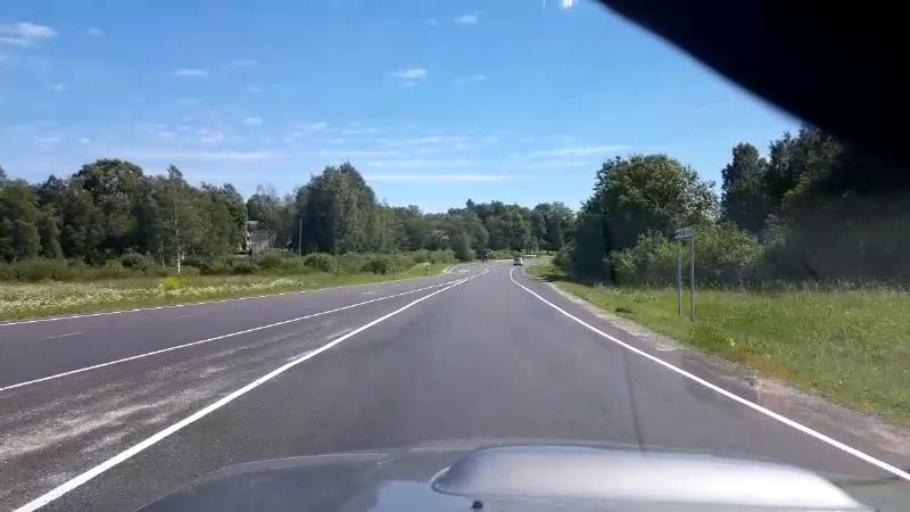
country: EE
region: Jaervamaa
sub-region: Jaerva-Jaani vald
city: Jarva-Jaani
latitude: 59.0478
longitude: 25.8786
